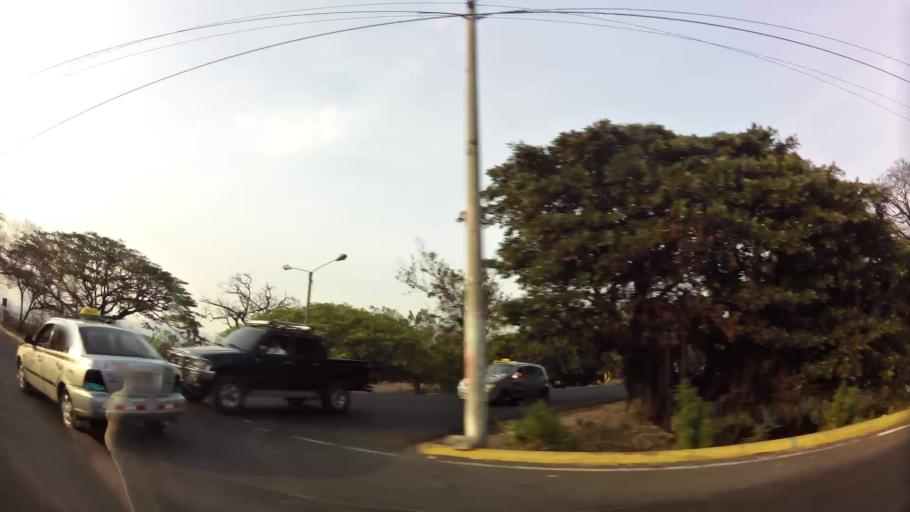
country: NI
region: Managua
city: Ciudad Sandino
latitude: 12.1322
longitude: -86.3133
